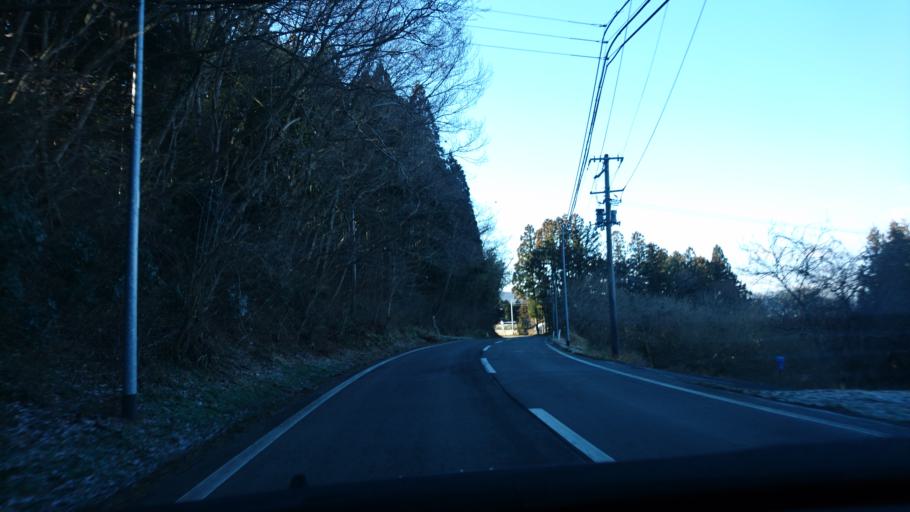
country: JP
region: Iwate
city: Ichinoseki
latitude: 38.8636
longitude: 141.2984
